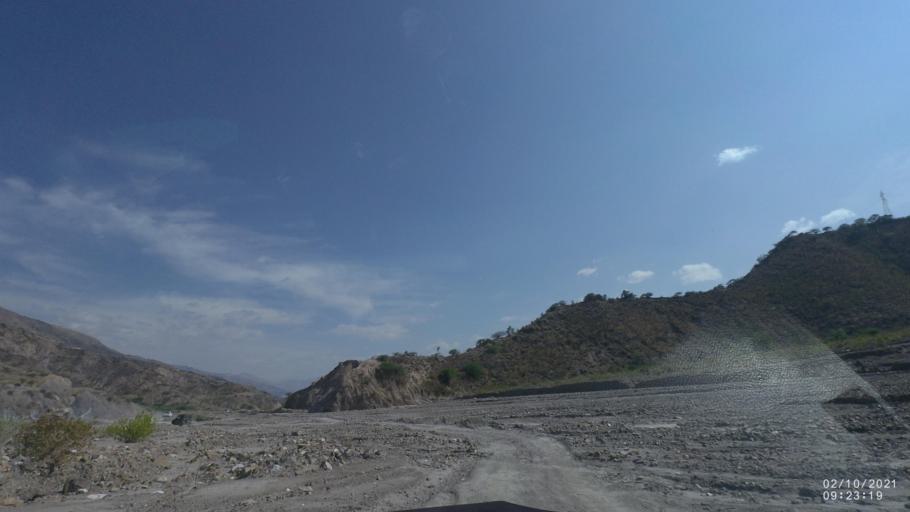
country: BO
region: Cochabamba
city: Irpa Irpa
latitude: -17.8684
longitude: -66.3105
